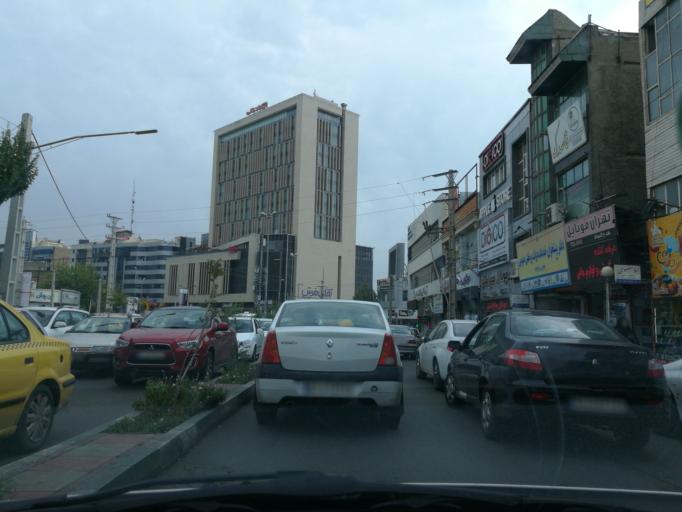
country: IR
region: Alborz
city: Karaj
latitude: 35.8449
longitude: 50.9708
